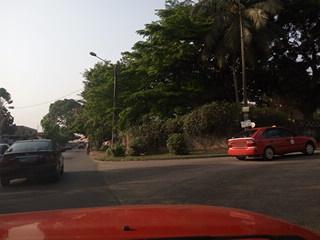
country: CI
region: Lagunes
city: Abobo
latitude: 5.3749
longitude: -3.9888
